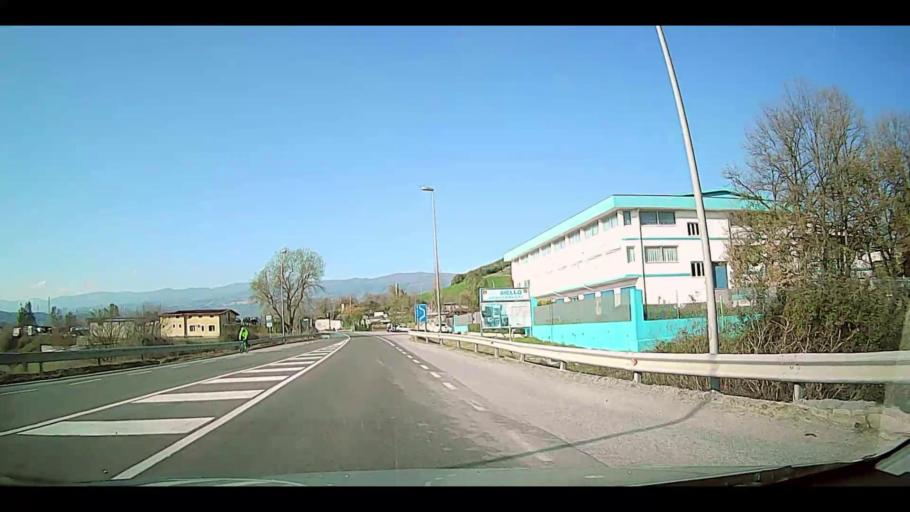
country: IT
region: Calabria
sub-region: Provincia di Crotone
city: Belvedere Spinello
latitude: 39.1886
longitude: 16.8473
